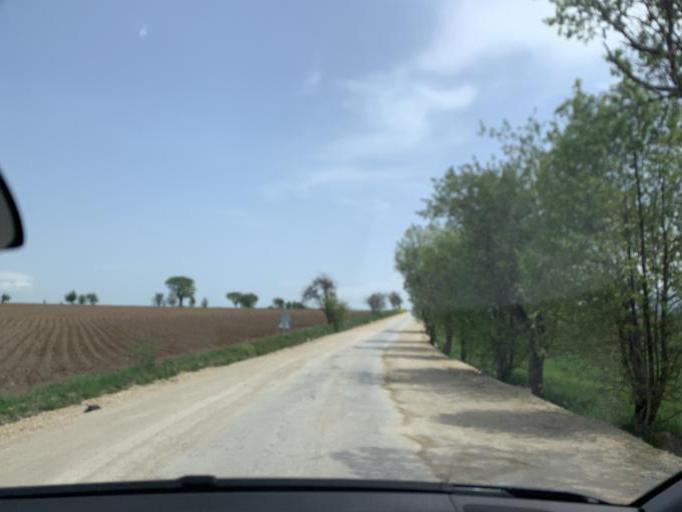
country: TR
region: Bolu
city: Bolu
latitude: 40.7583
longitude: 31.6833
